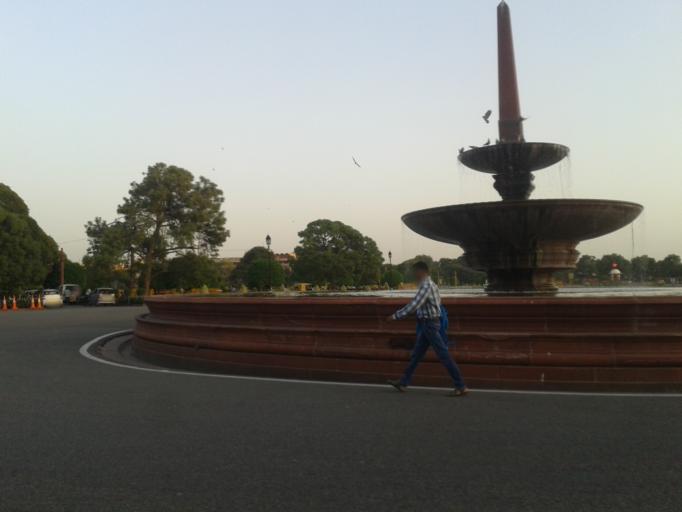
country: IN
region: NCT
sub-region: New Delhi
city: New Delhi
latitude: 28.6157
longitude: 77.2091
